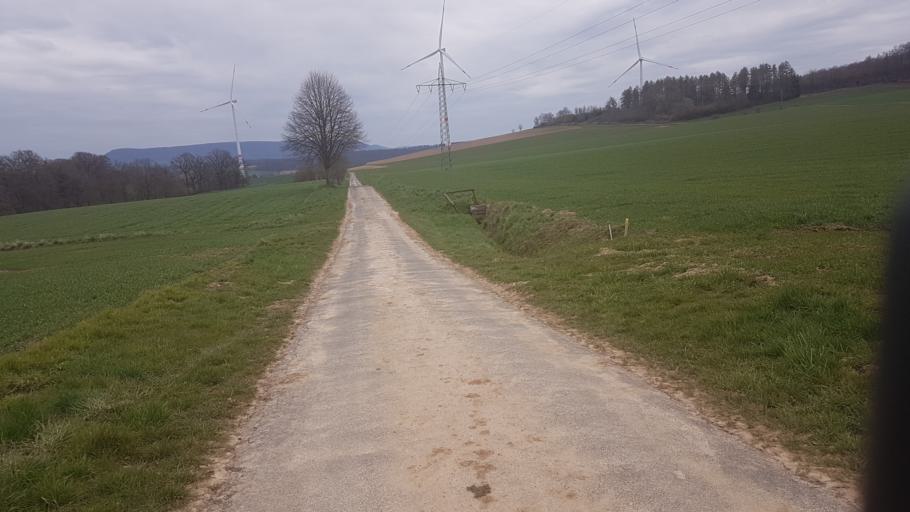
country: DE
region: Lower Saxony
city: Hameln
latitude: 52.1405
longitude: 9.4171
